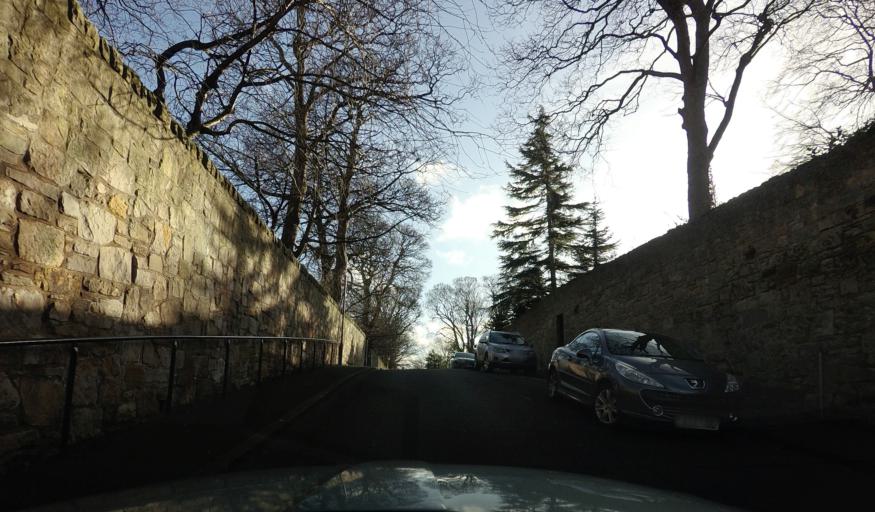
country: GB
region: Scotland
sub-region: Edinburgh
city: Edinburgh
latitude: 55.9792
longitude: -3.2016
